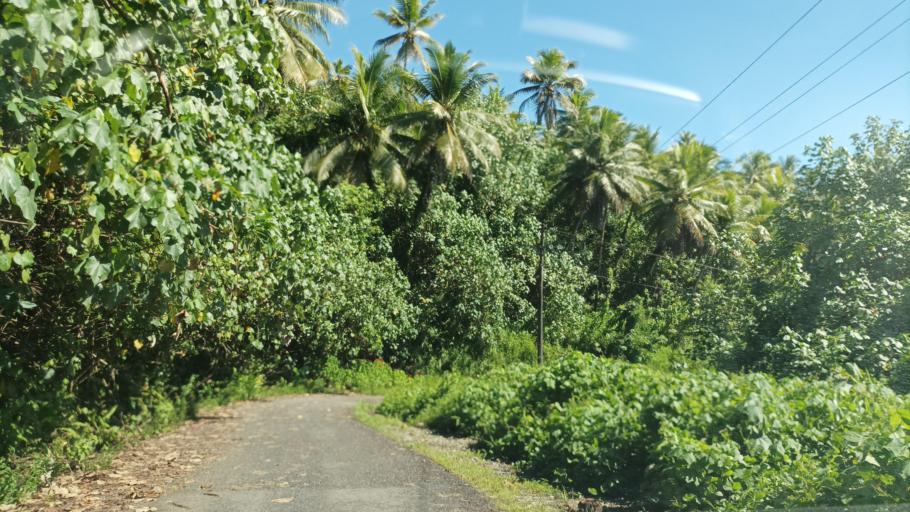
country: FM
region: Pohnpei
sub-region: Madolenihm Municipality
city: Madolenihm Municipality Government
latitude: 6.8494
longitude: 158.3179
